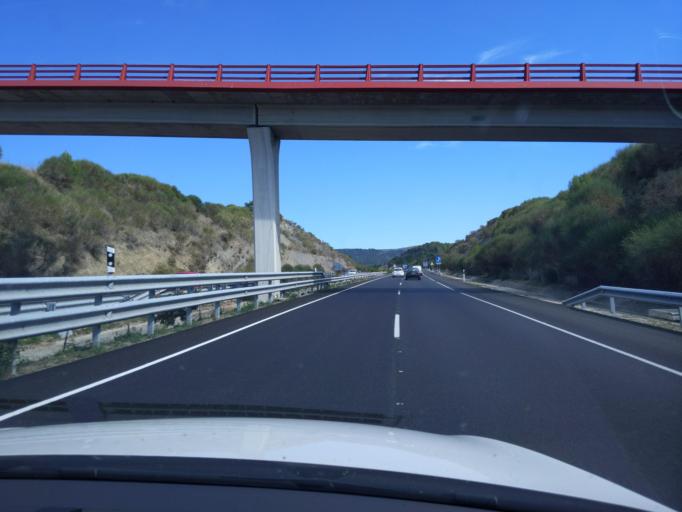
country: ES
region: Navarre
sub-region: Provincia de Navarra
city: Legarda
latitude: 42.7179
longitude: -1.7702
